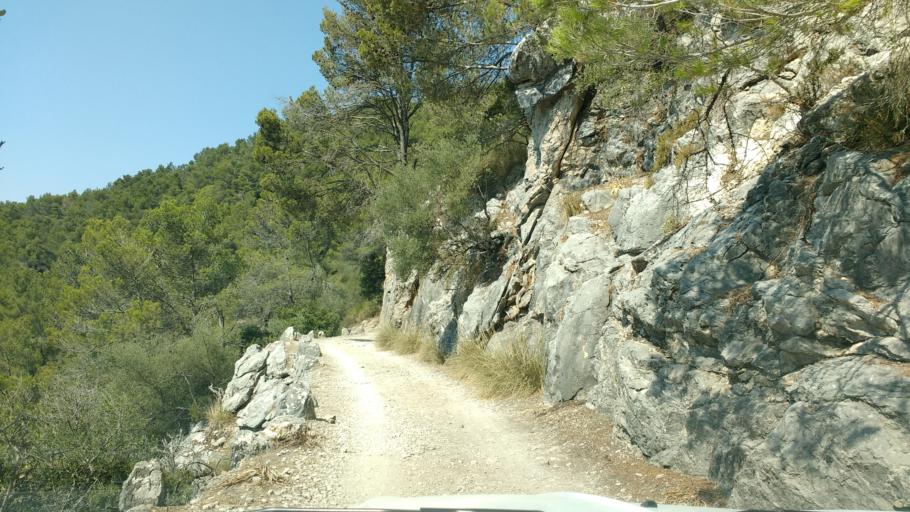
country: ES
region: Balearic Islands
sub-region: Illes Balears
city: Alaro
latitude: 39.7341
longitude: 2.7861
